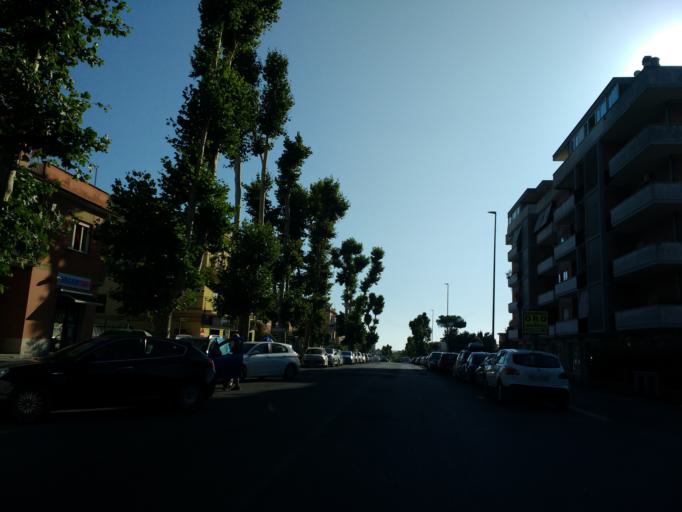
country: IT
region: Latium
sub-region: Citta metropolitana di Roma Capitale
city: Acilia-Castel Fusano-Ostia Antica
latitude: 41.7808
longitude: 12.3639
